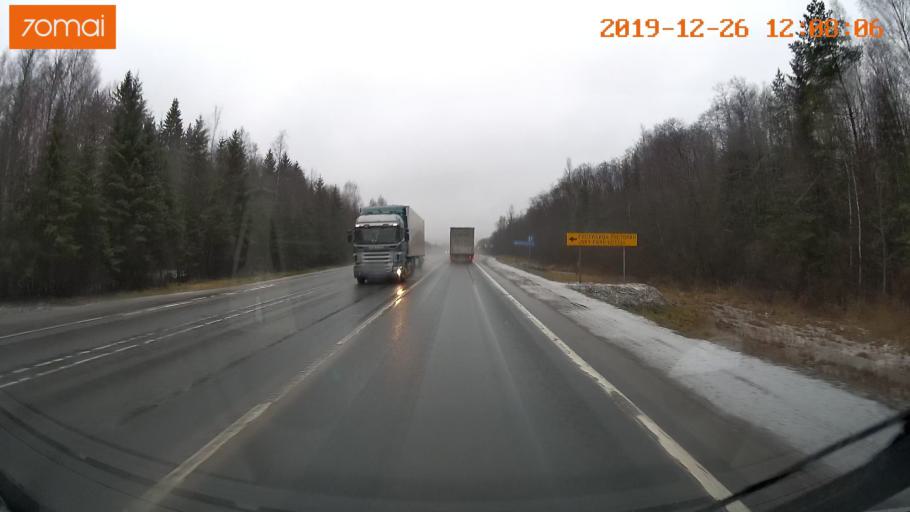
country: RU
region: Vologda
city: Tonshalovo
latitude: 59.2855
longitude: 38.0198
